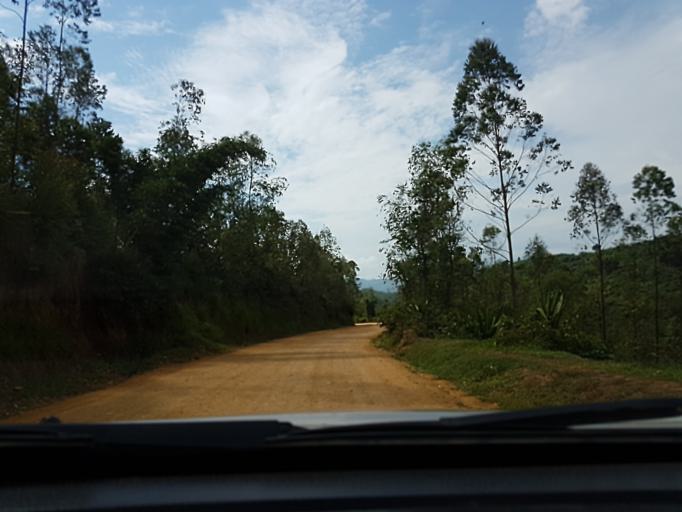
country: CD
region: South Kivu
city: Bukavu
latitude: -2.6290
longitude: 28.8748
